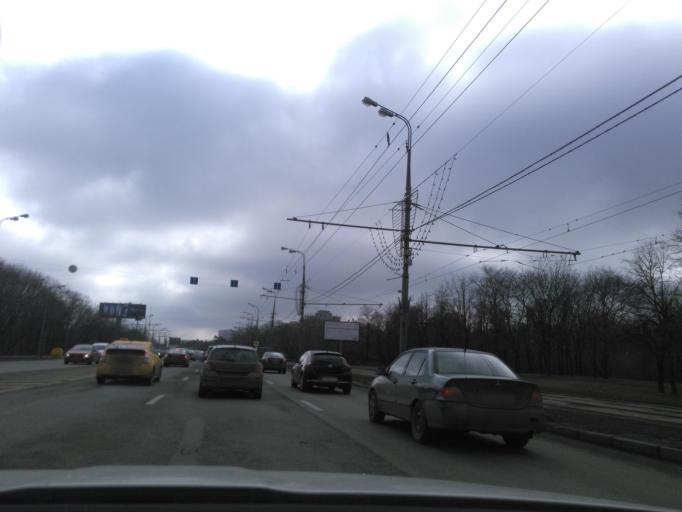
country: RU
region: Moscow
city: Pokrovskoye-Streshnevo
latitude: 55.8141
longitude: 37.4706
